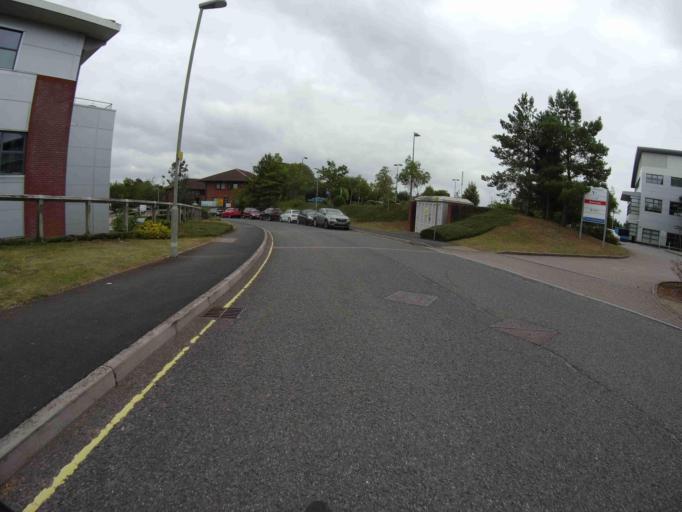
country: GB
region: England
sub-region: Devon
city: Heavitree
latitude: 50.7095
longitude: -3.4862
